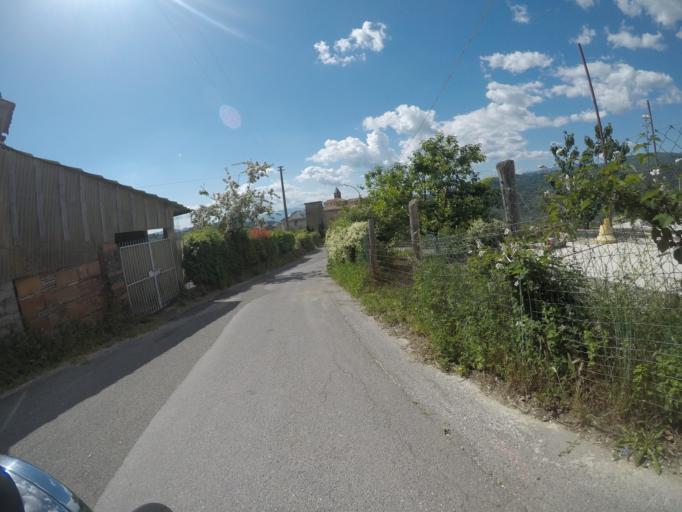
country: IT
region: Tuscany
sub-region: Provincia di Massa-Carrara
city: Casola in Lunigiana
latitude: 44.1813
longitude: 10.1578
